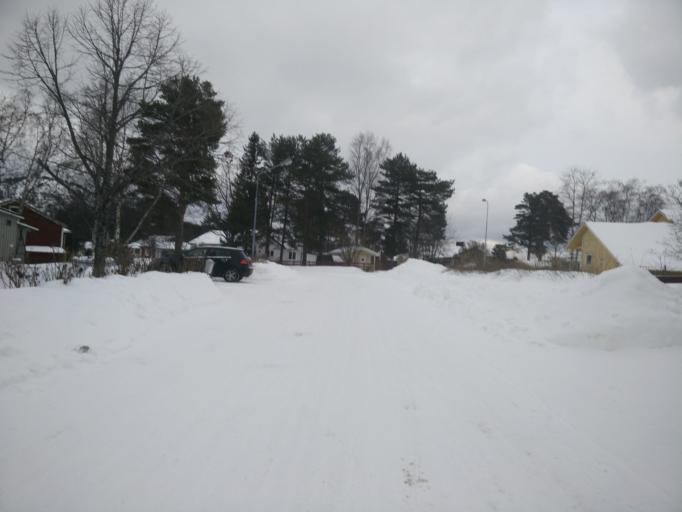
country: SE
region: Vaesternorrland
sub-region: Sundsvalls Kommun
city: Nolby
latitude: 62.2885
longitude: 17.3620
